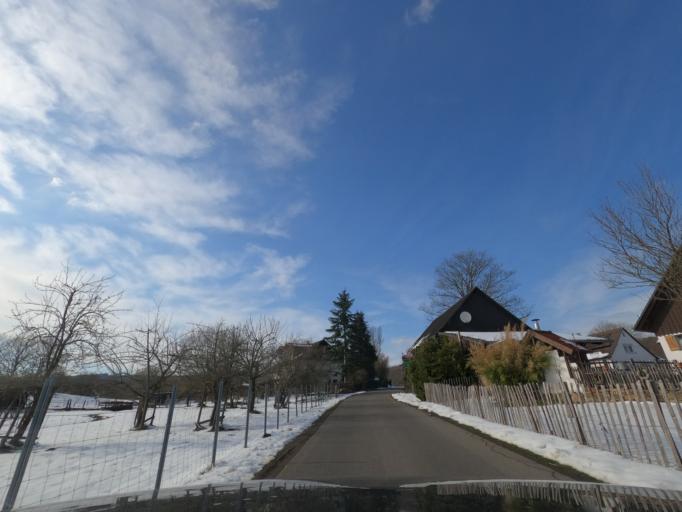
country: DE
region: North Rhine-Westphalia
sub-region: Regierungsbezirk Arnsberg
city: Herscheid
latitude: 51.1234
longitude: 7.7748
